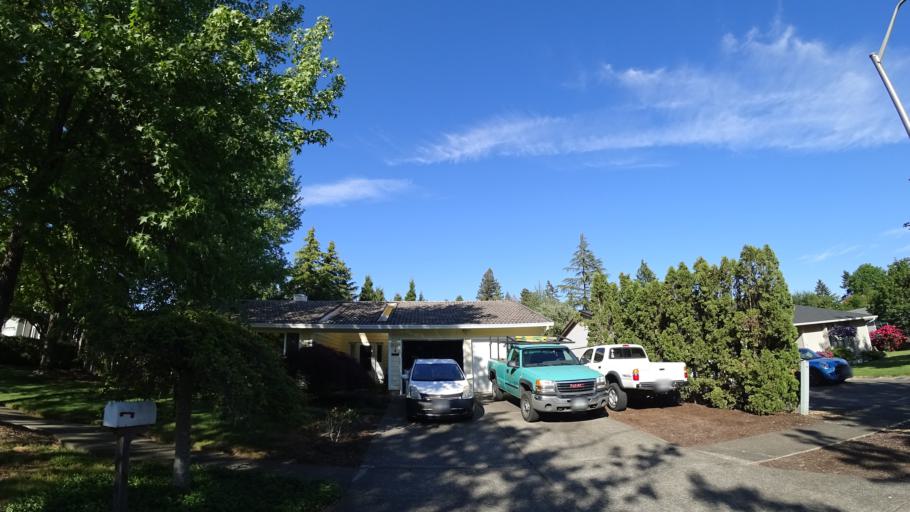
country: US
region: Oregon
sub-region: Washington County
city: Beaverton
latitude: 45.4573
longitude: -122.8099
